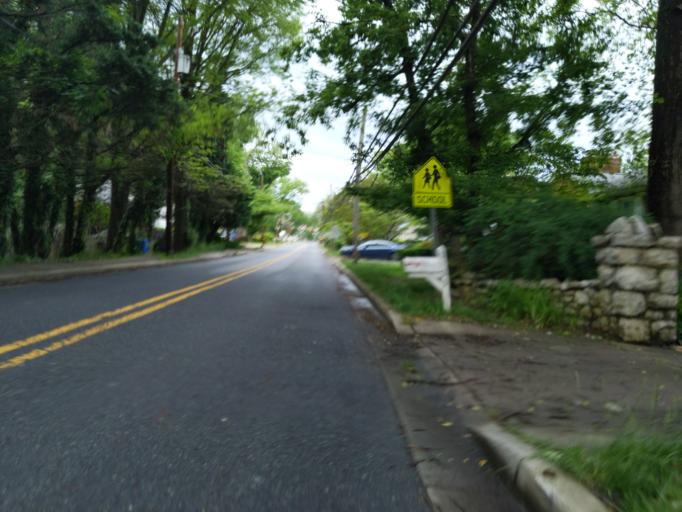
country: US
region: Maryland
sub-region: Montgomery County
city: Forest Glen
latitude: 39.0093
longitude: -77.0475
